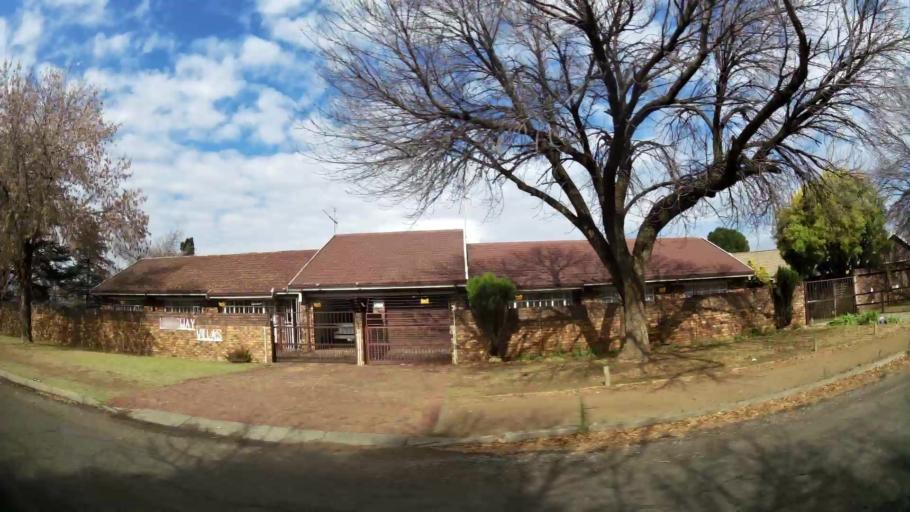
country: ZA
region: Gauteng
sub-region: Sedibeng District Municipality
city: Vereeniging
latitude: -26.6539
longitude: 27.9771
